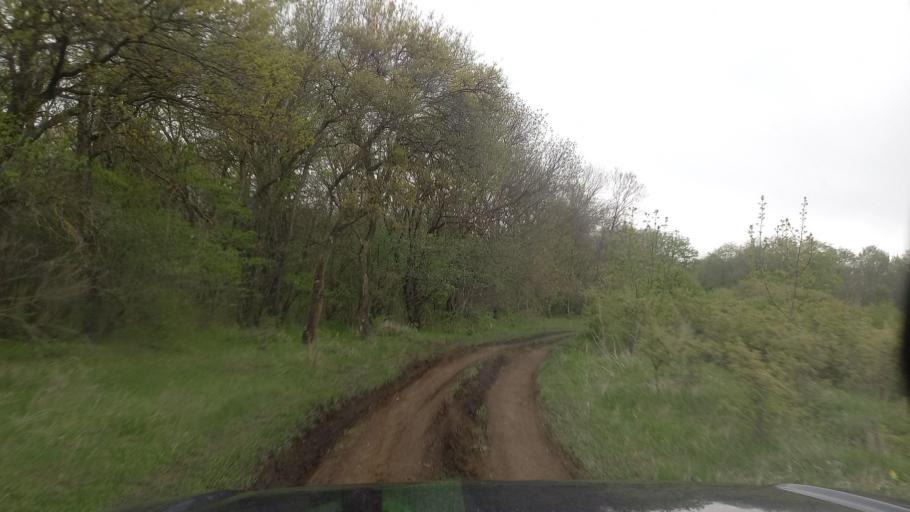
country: RU
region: Stavropol'skiy
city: Nezhinskiy
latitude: 43.8795
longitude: 42.6835
